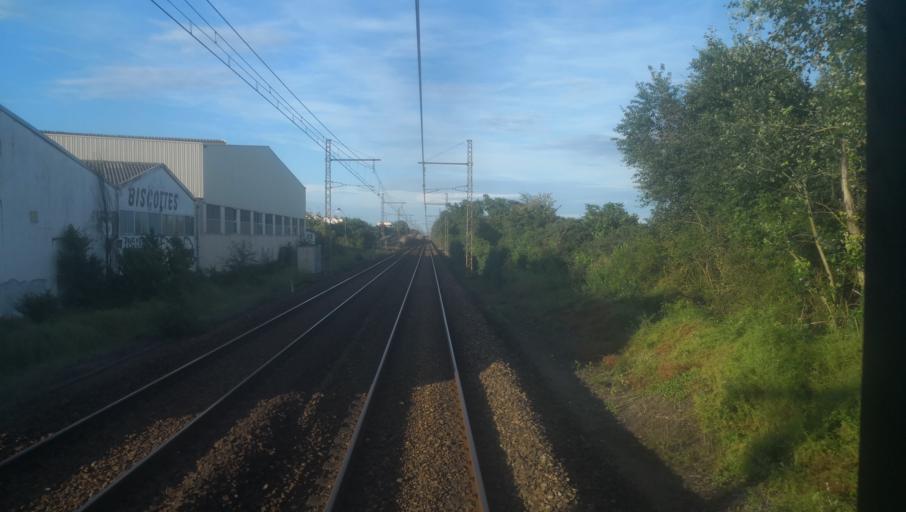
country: FR
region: Centre
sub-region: Departement de l'Indre
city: Saint-Maur
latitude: 46.7965
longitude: 1.6683
